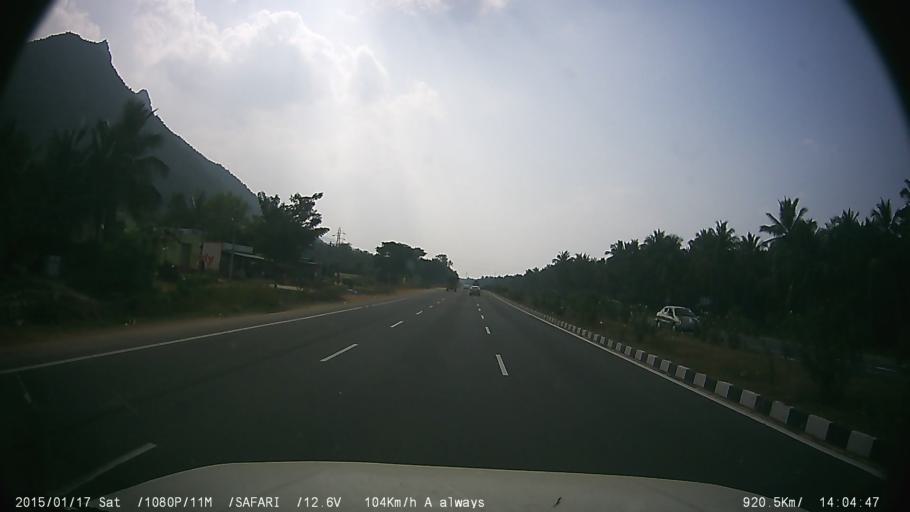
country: IN
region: Tamil Nadu
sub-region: Vellore
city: Odugattur
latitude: 12.8527
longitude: 78.8159
